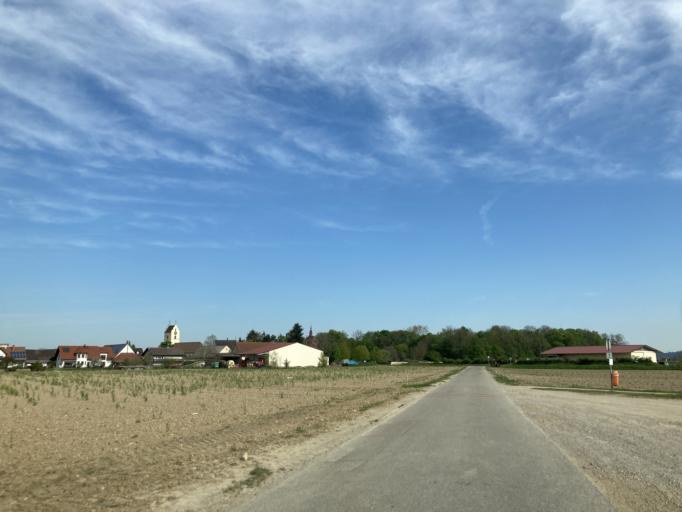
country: DE
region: Baden-Wuerttemberg
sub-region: Freiburg Region
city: Hartheim
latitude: 47.9333
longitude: 7.6521
